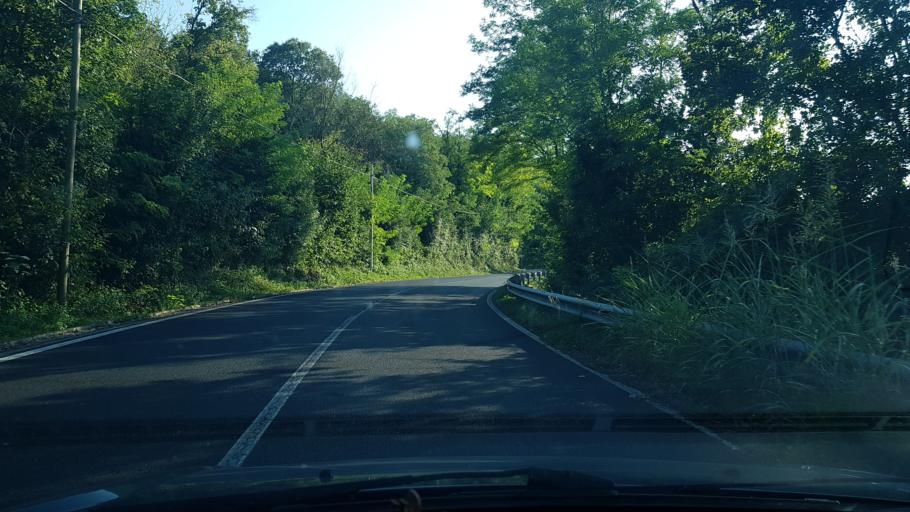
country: IT
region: Friuli Venezia Giulia
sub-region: Provincia di Gorizia
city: Farra d'Isonzo
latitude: 45.8940
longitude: 13.5346
